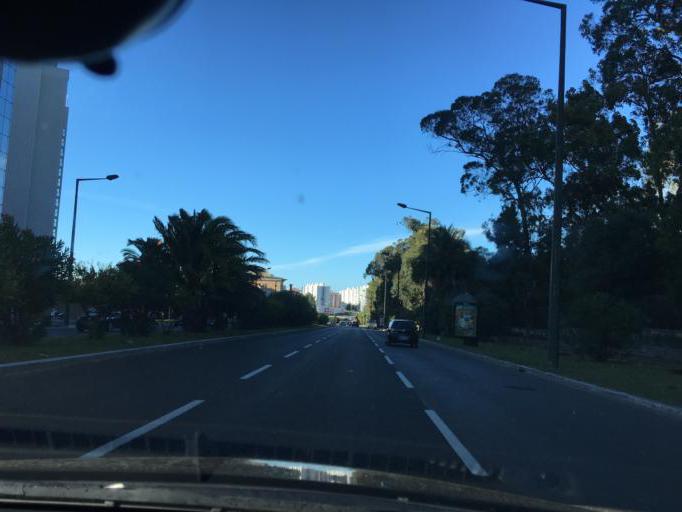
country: PT
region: Lisbon
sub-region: Lisbon
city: Lisbon
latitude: 38.7464
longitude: -9.1627
